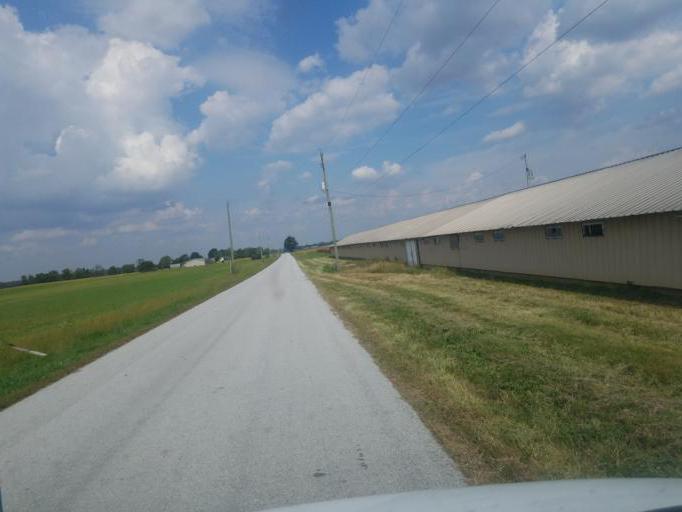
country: US
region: Ohio
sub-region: Hardin County
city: Kenton
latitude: 40.6243
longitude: -83.6516
